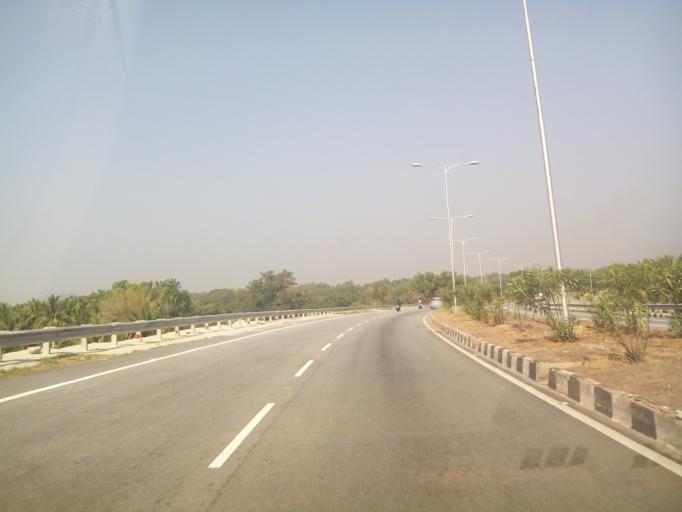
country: IN
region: Karnataka
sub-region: Tumkur
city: Kunigal
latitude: 13.0002
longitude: 77.0218
